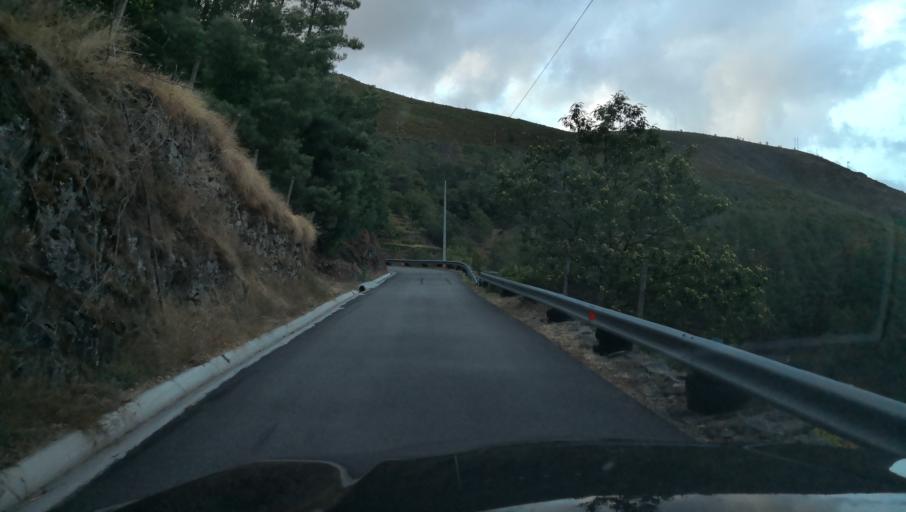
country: PT
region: Vila Real
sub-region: Santa Marta de Penaguiao
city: Santa Marta de Penaguiao
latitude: 41.2681
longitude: -7.8740
